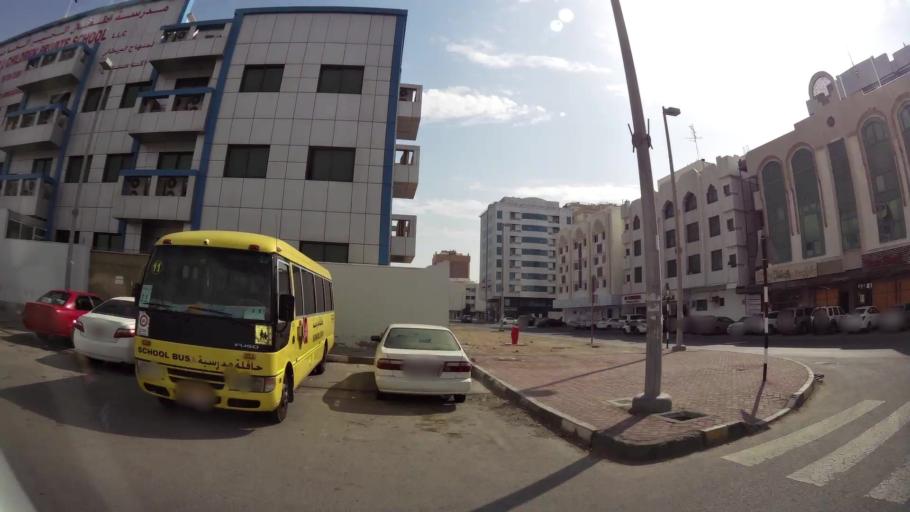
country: AE
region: Abu Dhabi
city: Abu Dhabi
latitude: 24.3306
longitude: 54.5369
